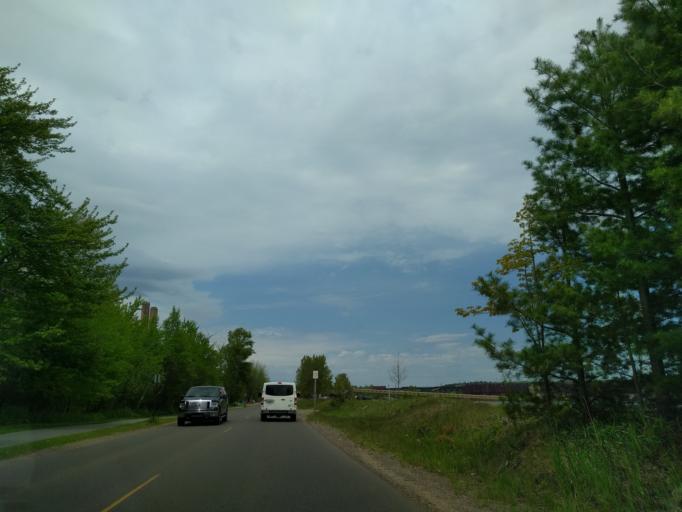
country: US
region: Michigan
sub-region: Marquette County
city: Marquette
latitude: 46.5728
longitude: -87.3935
